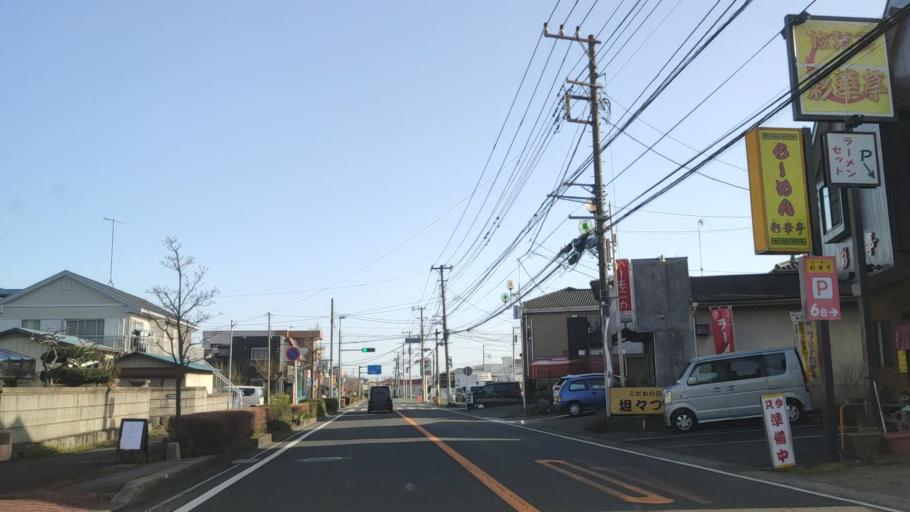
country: JP
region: Kanagawa
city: Zama
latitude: 35.5084
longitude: 139.3394
